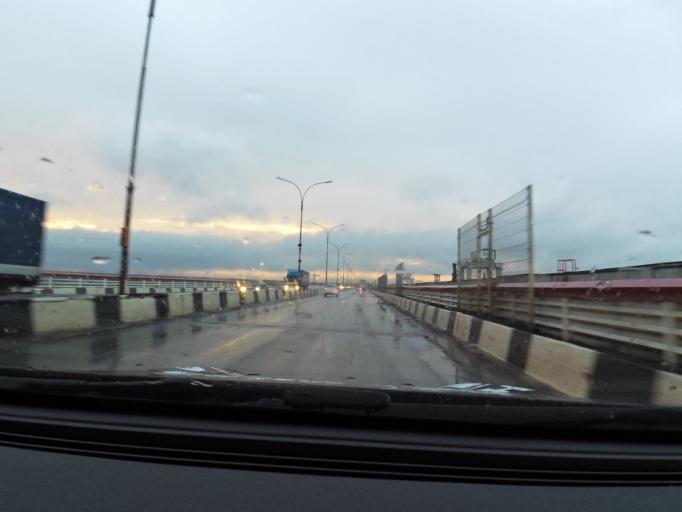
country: RU
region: Tatarstan
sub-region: Tukayevskiy Rayon
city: Naberezhnyye Chelny
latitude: 55.6982
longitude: 52.2790
